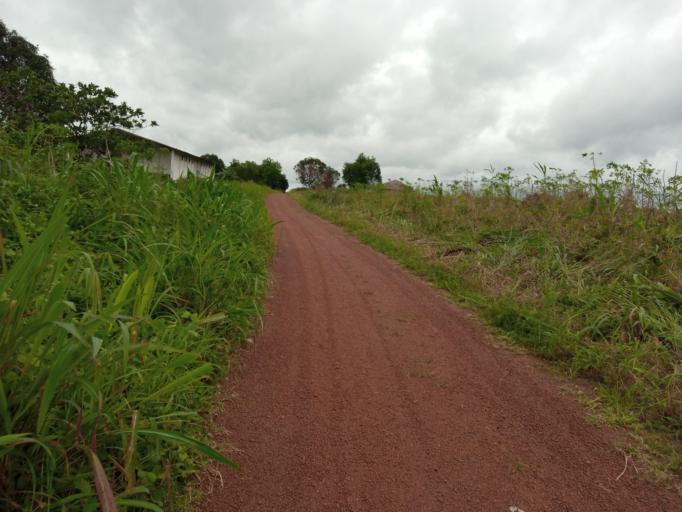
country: SL
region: Southern Province
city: Largo
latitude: 8.1977
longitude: -12.0492
